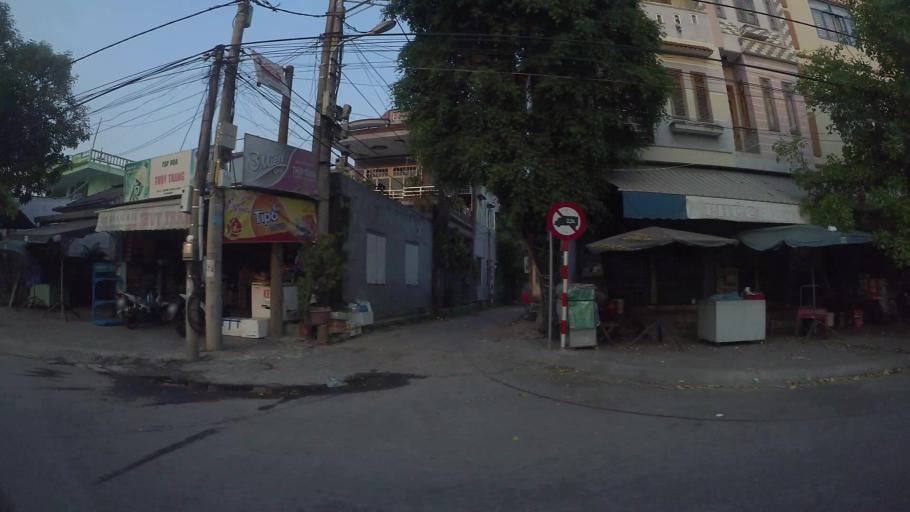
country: VN
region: Da Nang
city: Cam Le
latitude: 15.9498
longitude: 108.2193
